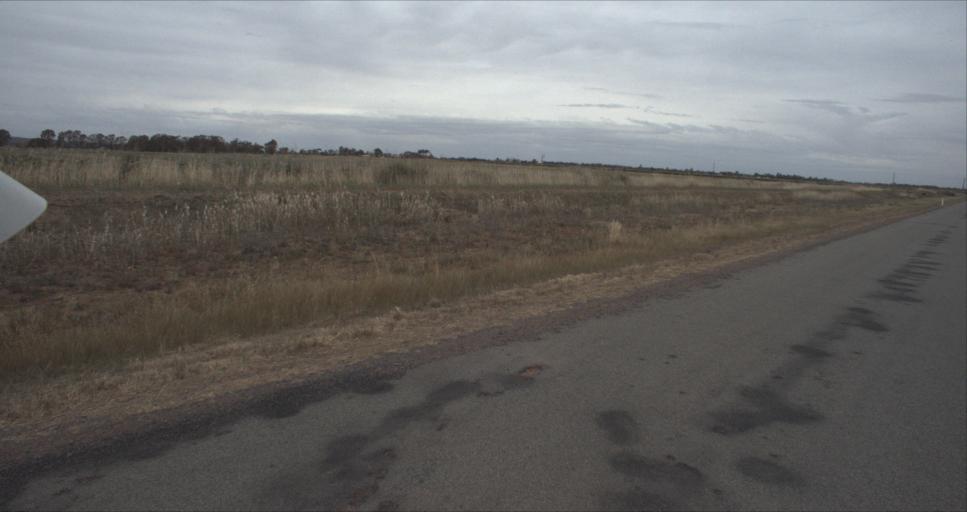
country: AU
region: New South Wales
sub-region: Leeton
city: Leeton
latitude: -34.4979
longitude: 146.4002
